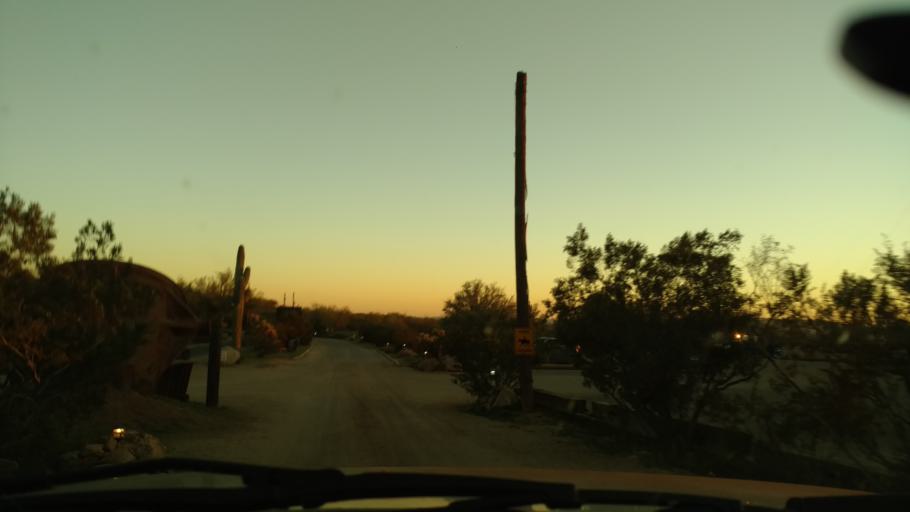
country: US
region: Arizona
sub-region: Pinal County
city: Apache Junction
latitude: 33.4559
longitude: -111.4921
